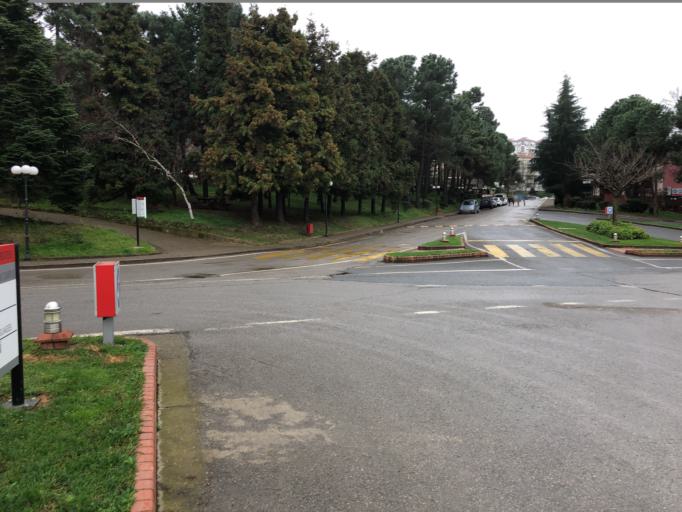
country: TR
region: Trabzon
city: Trabzon
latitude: 40.9976
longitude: 39.7688
